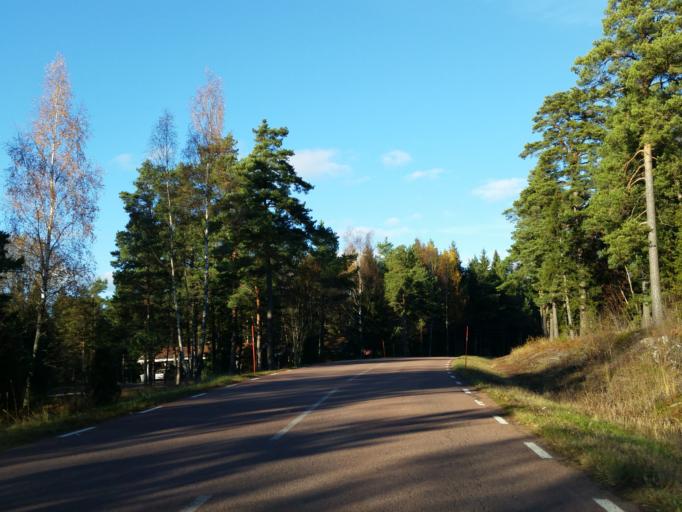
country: AX
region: Alands landsbygd
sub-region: Finstroem
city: Finstroem
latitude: 60.3163
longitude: 19.9411
